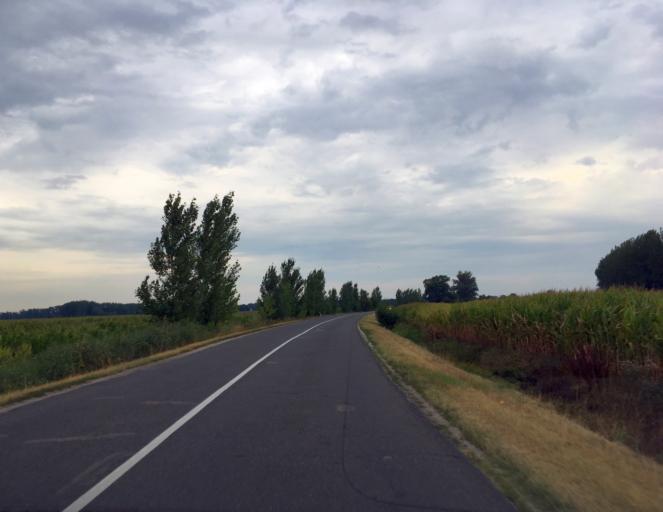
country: SK
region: Trnavsky
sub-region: Okres Dunajska Streda
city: Velky Meder
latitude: 47.9000
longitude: 17.6794
